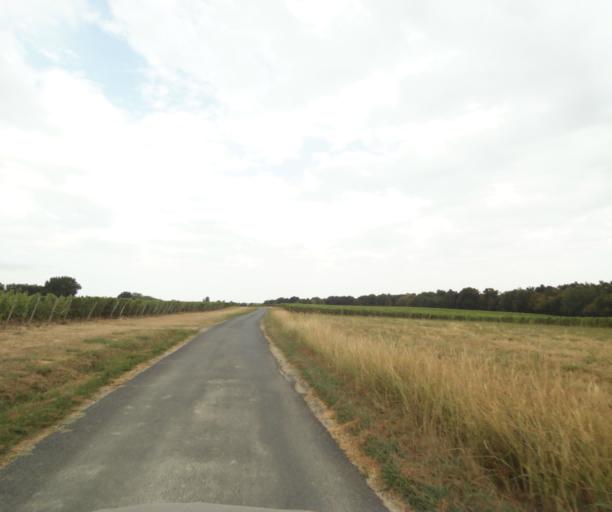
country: FR
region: Aquitaine
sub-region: Departement de la Gironde
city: Creon
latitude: 44.7515
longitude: -0.3394
